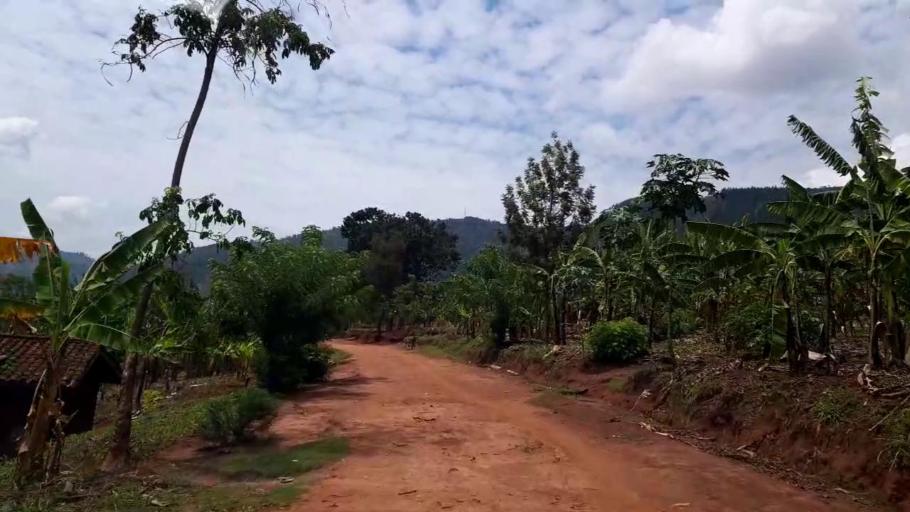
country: RW
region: Northern Province
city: Byumba
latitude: -1.4927
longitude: 30.1961
